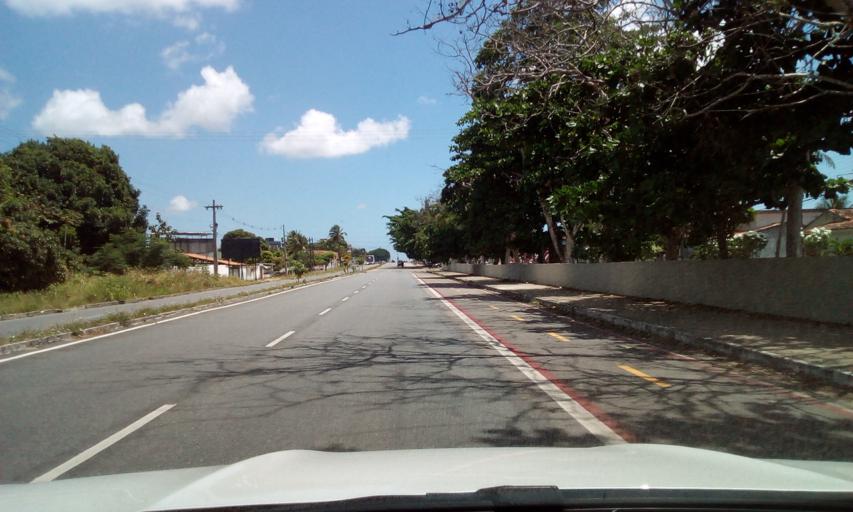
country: BR
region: Paraiba
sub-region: Bayeux
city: Bayeux
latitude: -7.1370
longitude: -34.9416
